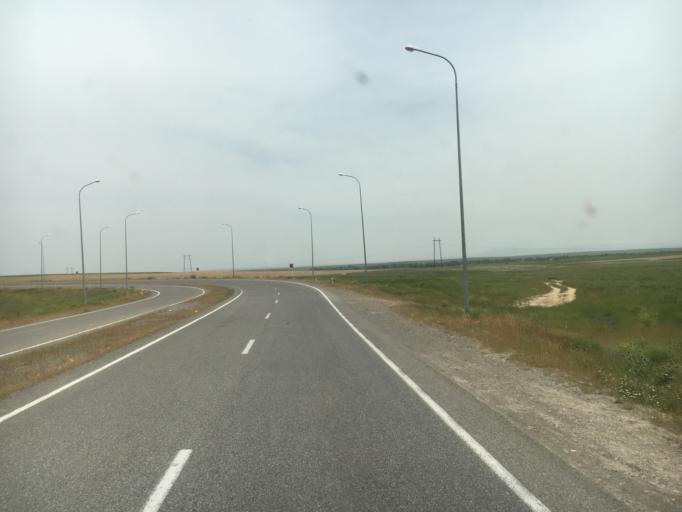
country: KZ
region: Ongtustik Qazaqstan
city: Temirlanovka
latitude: 42.5287
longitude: 69.3456
